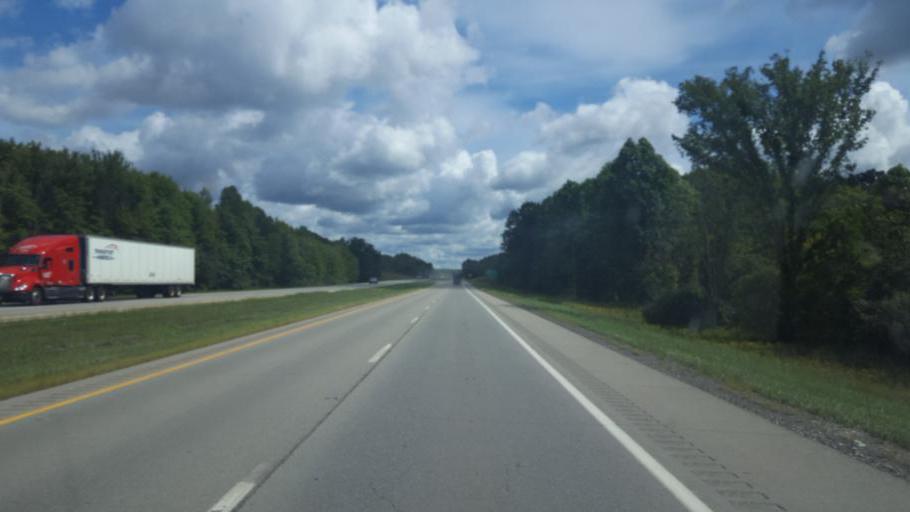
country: US
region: Ohio
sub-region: Lorain County
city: Elyria
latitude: 41.3085
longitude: -82.1401
